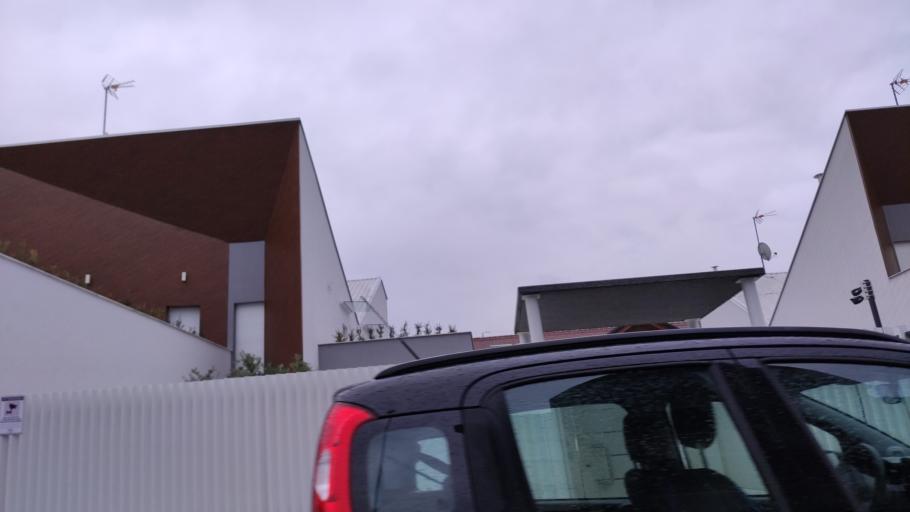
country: IT
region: Piedmont
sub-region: Provincia di Torino
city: Settimo Torinese
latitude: 45.1365
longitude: 7.7516
